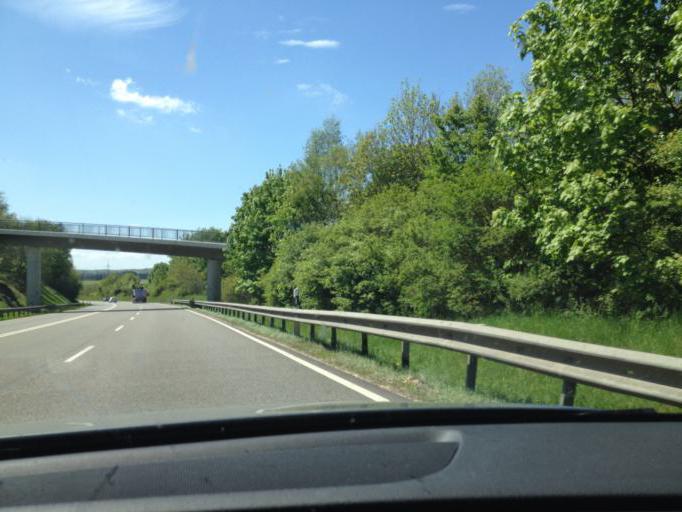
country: DE
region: North Rhine-Westphalia
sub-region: Regierungsbezirk Koln
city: Blankenheim
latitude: 50.4493
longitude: 6.6292
